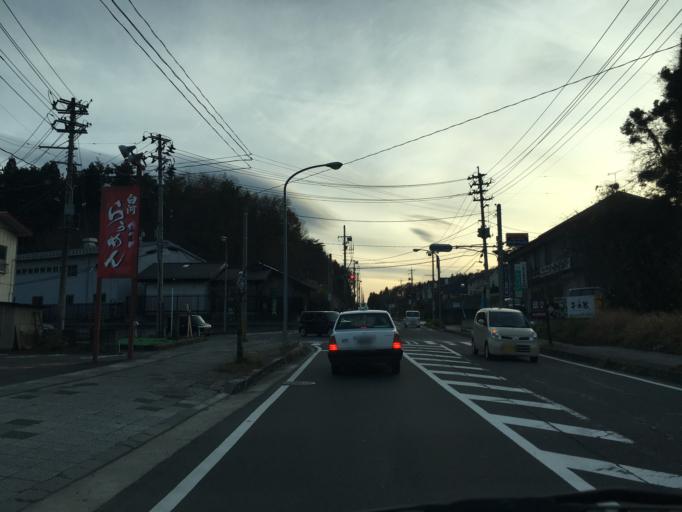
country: JP
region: Fukushima
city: Ishikawa
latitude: 37.1142
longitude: 140.2267
